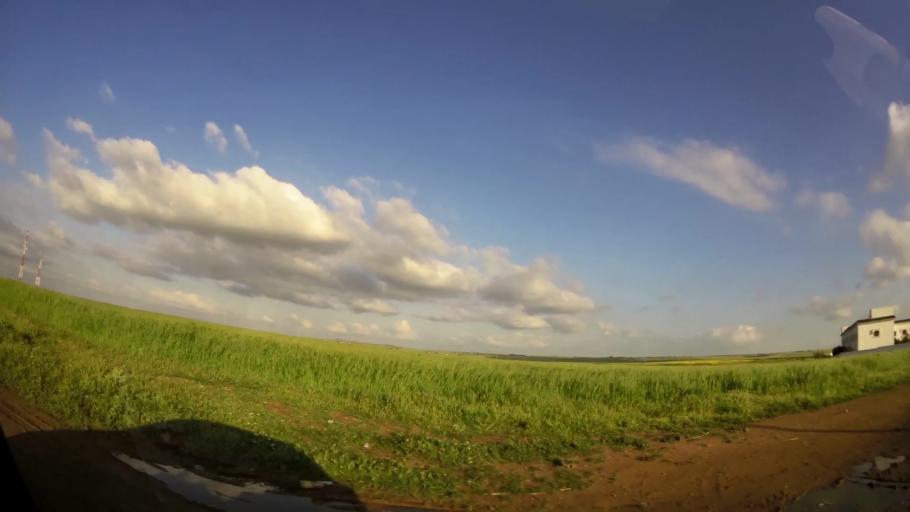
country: MA
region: Chaouia-Ouardigha
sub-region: Settat Province
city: Settat
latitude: 33.0074
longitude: -7.5942
